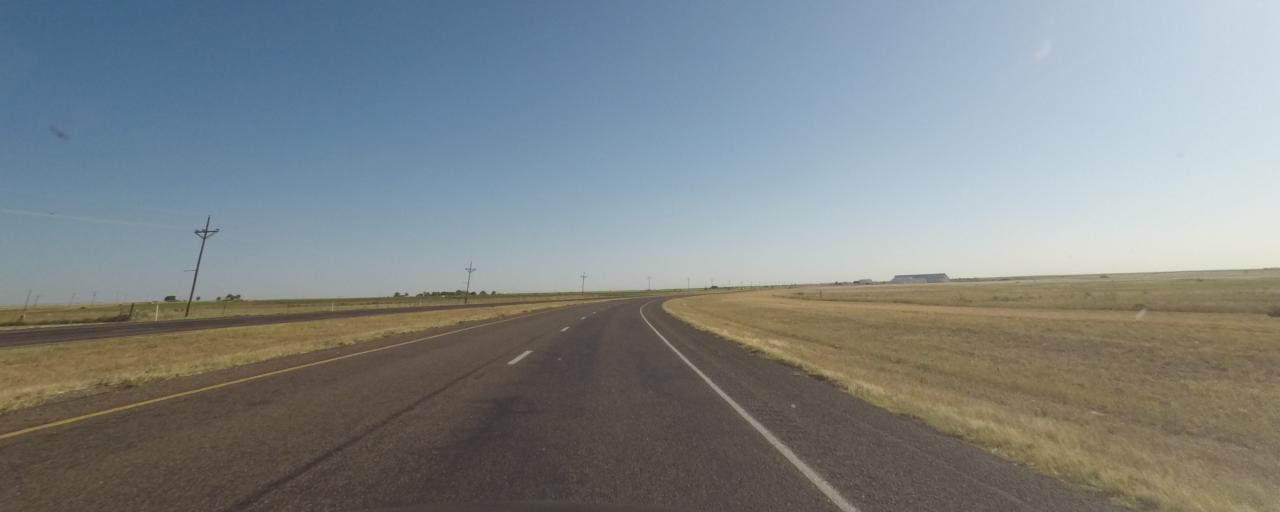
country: US
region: Texas
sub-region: Gaines County
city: Seagraves
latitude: 32.8732
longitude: -102.6392
